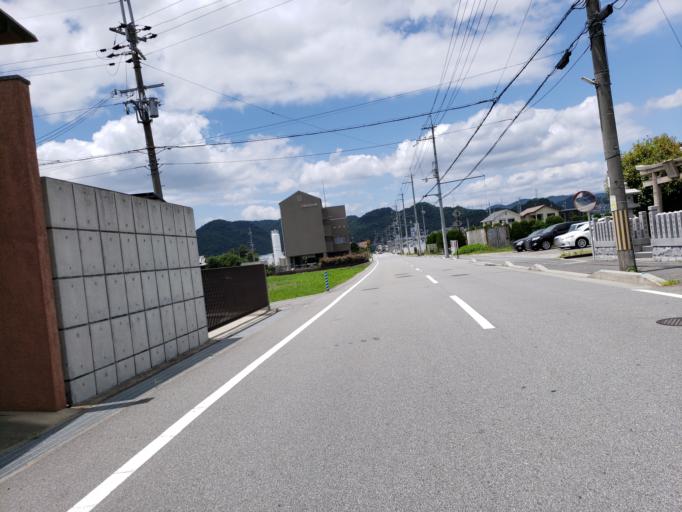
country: JP
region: Hyogo
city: Himeji
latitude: 34.8835
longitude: 134.7396
